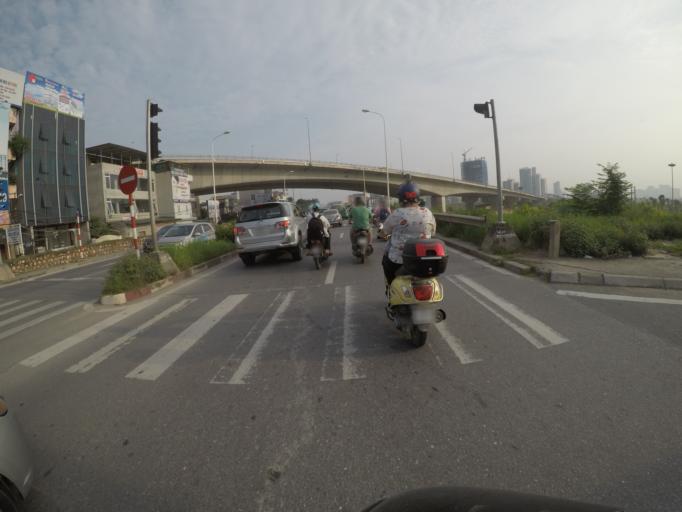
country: VN
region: Ha Noi
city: Tay Ho
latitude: 21.0855
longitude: 105.8163
